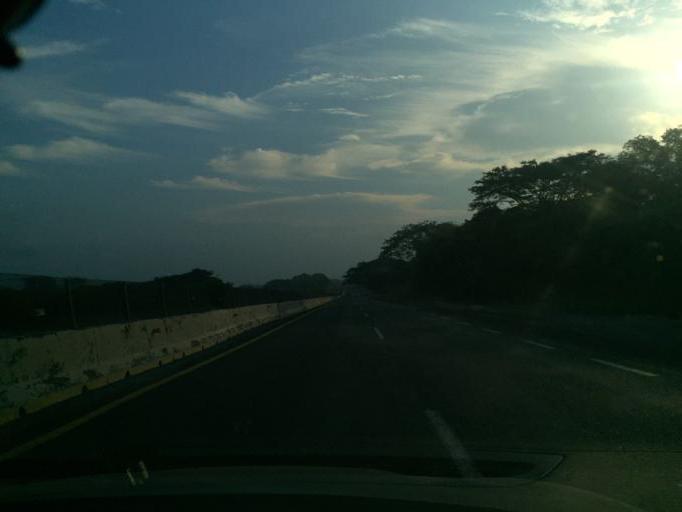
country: MX
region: Veracruz
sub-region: Tierra Blanca
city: Huixcolotla
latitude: 18.7854
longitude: -96.5152
